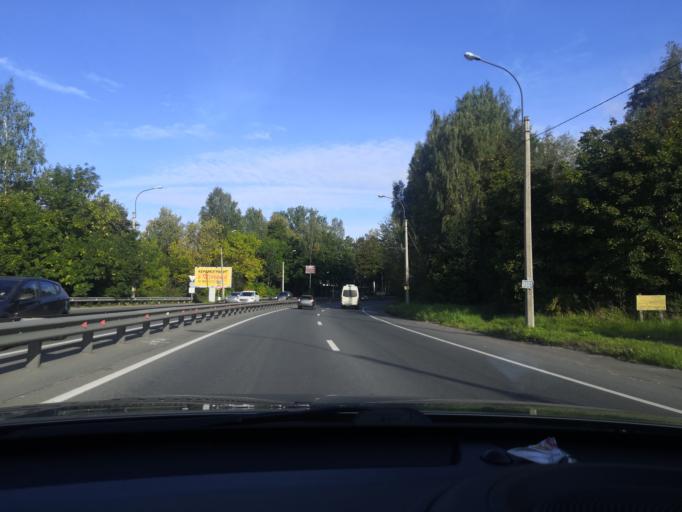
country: RU
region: St.-Petersburg
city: Pargolovo
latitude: 60.0799
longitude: 30.2649
